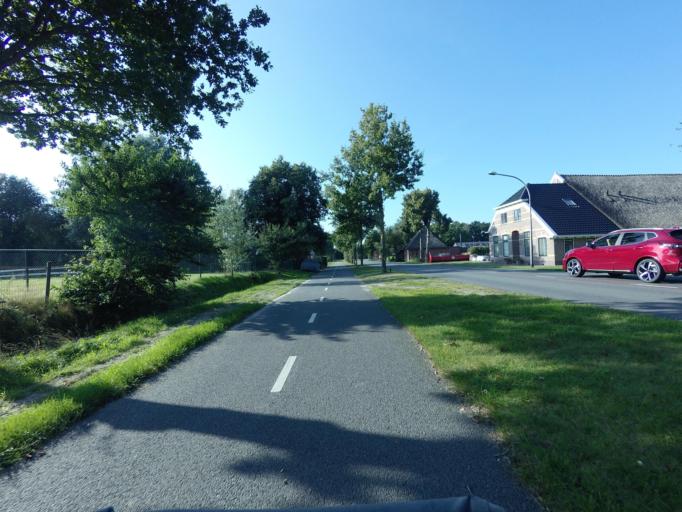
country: NL
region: Drenthe
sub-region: Gemeente Tynaarlo
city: Vries
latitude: 53.0943
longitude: 6.5501
